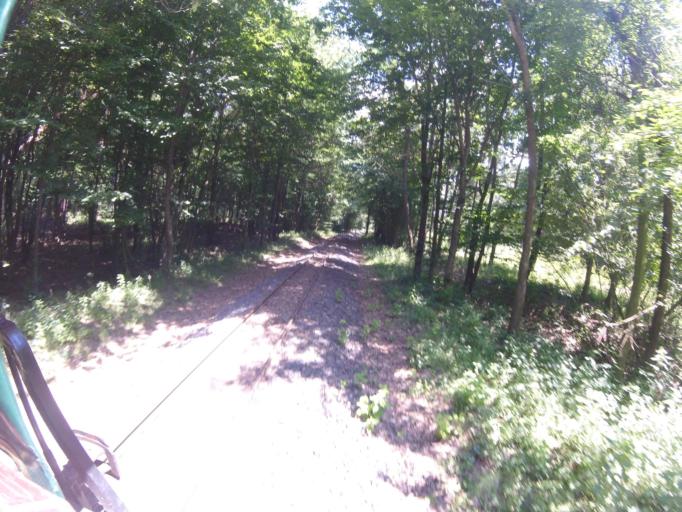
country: HU
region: Zala
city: Letenye
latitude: 46.5680
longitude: 16.7055
